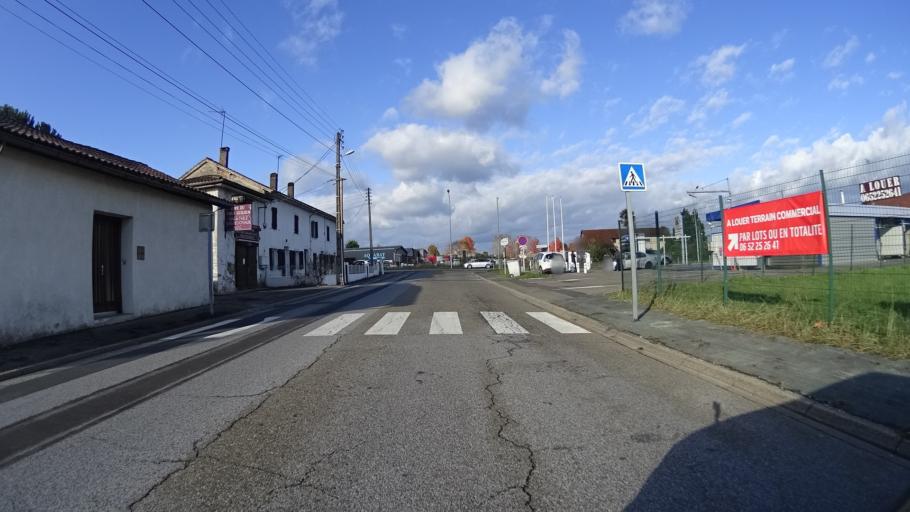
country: FR
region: Aquitaine
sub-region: Departement des Landes
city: Saint-Paul-les-Dax
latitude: 43.7267
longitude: -1.0837
